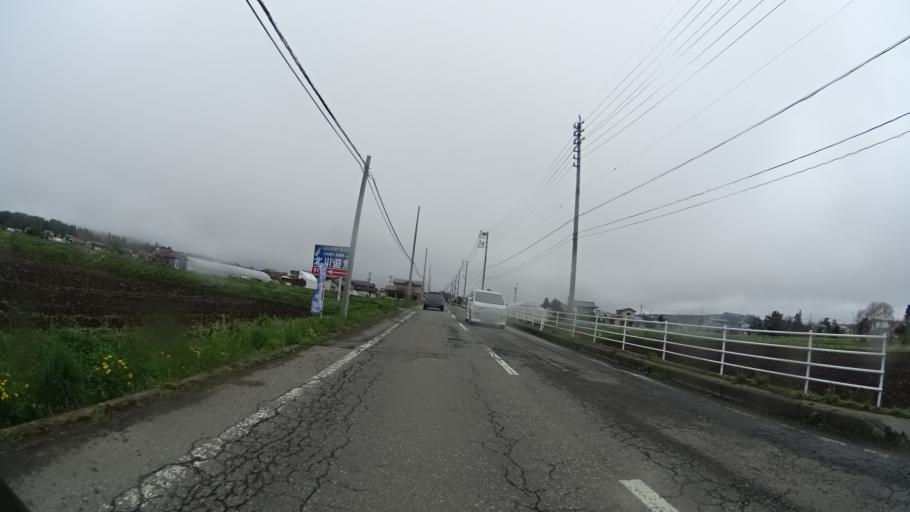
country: JP
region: Nagano
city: Nagano-shi
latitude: 36.7878
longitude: 138.1976
